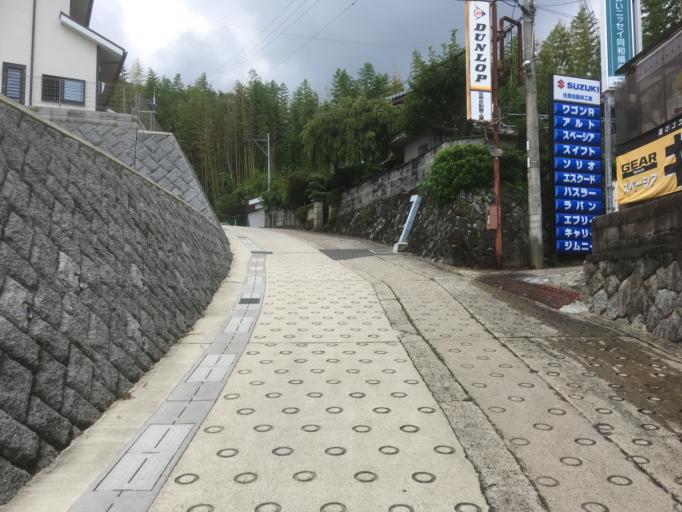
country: JP
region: Nara
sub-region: Ikoma-shi
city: Ikoma
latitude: 34.6675
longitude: 135.6924
